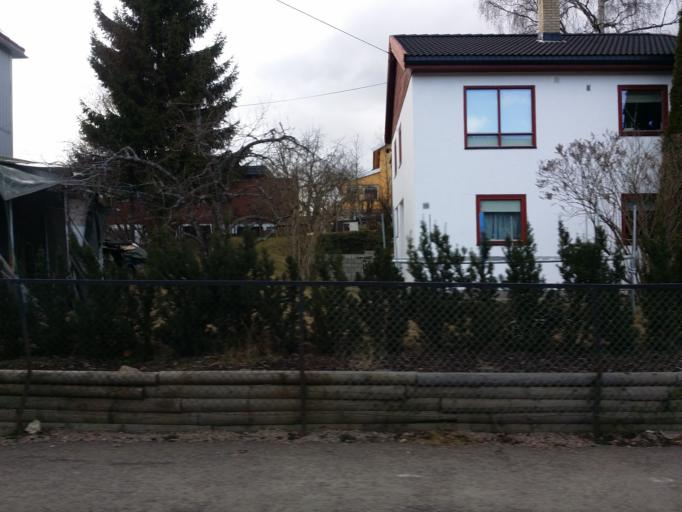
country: NO
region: Oslo
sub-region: Oslo
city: Oslo
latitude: 59.9563
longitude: 10.7857
